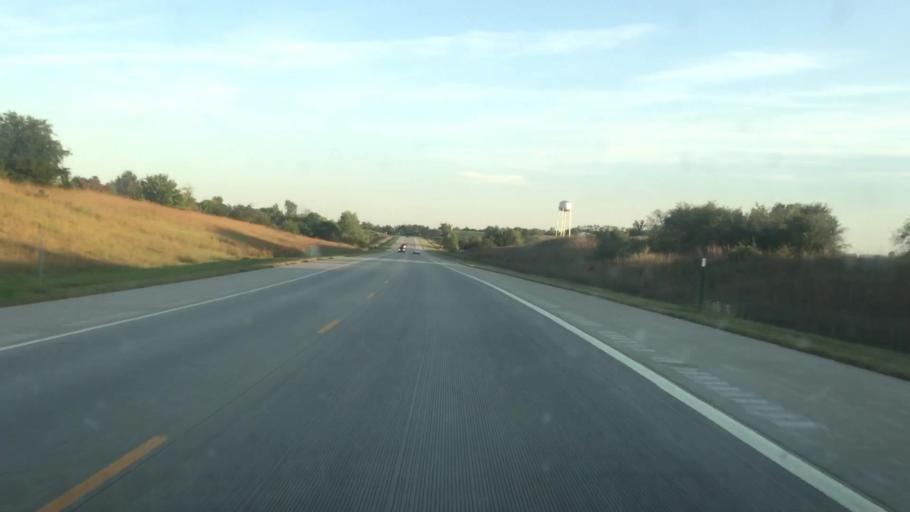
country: US
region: Kansas
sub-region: Leavenworth County
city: Leavenworth
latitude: 39.3771
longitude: -95.0563
